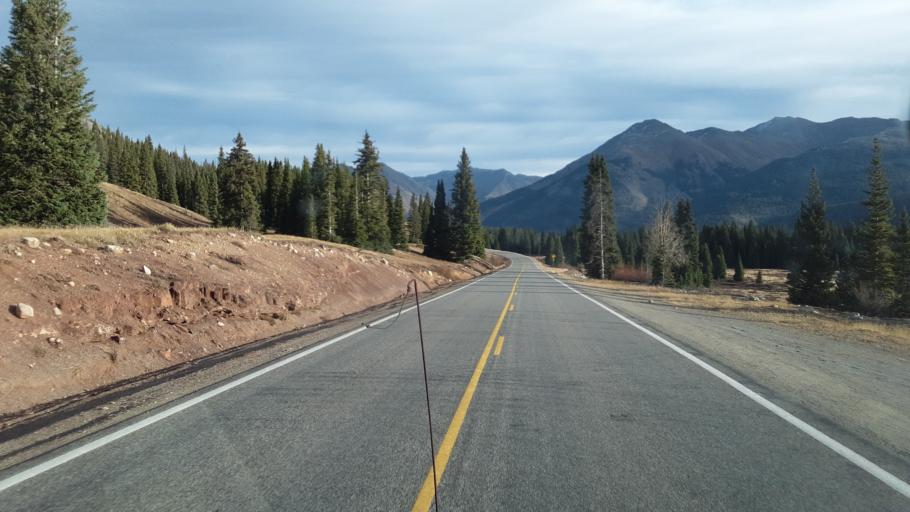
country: US
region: Colorado
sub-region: San Juan County
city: Silverton
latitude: 37.7527
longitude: -107.6829
